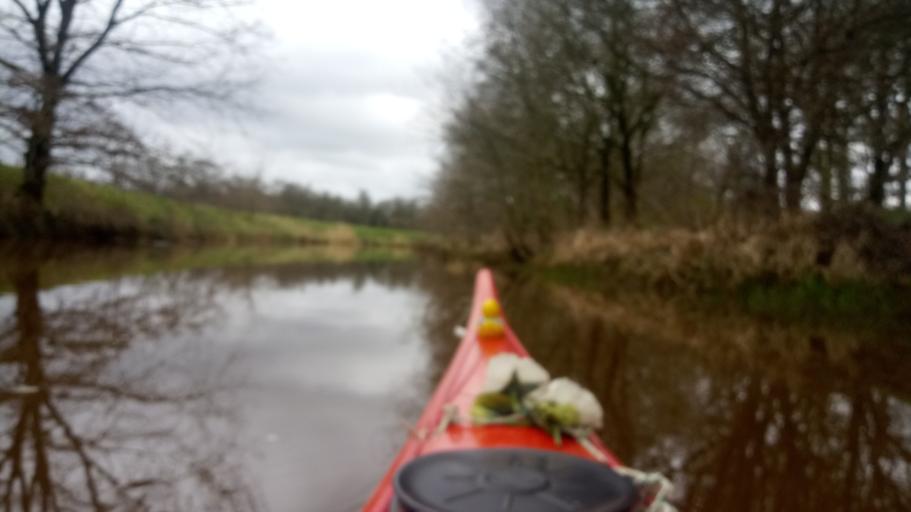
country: NL
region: Groningen
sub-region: Gemeente Vlagtwedde
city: Sellingen
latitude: 52.9431
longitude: 7.1329
